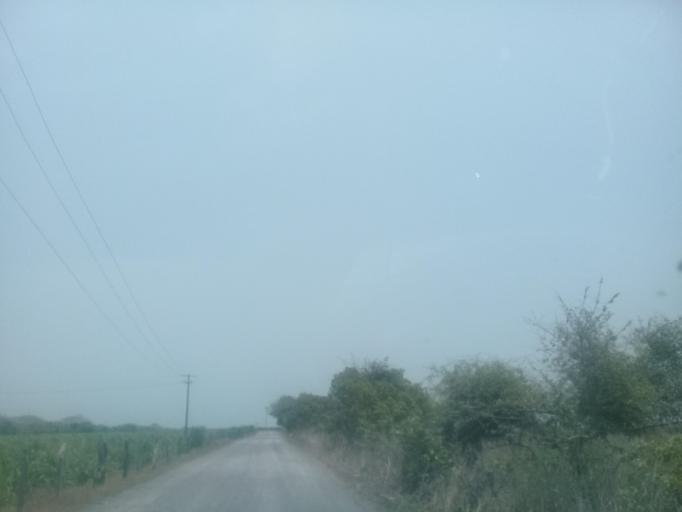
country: MX
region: Veracruz
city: Jamapa
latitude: 19.0971
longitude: -96.2355
